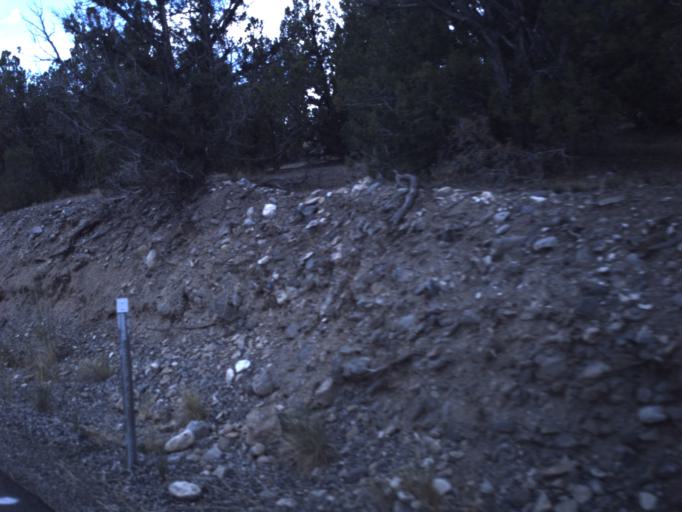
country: US
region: Utah
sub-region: Tooele County
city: Grantsville
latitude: 40.3350
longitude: -112.5271
